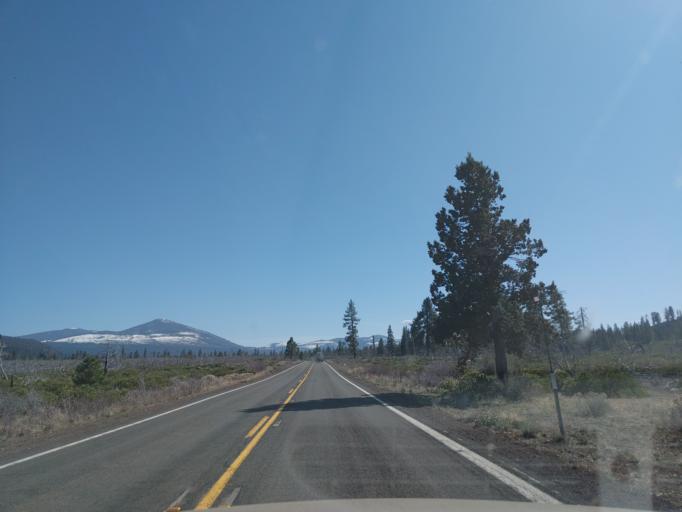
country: US
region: California
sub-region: Shasta County
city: Burney
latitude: 40.6986
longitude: -121.4180
